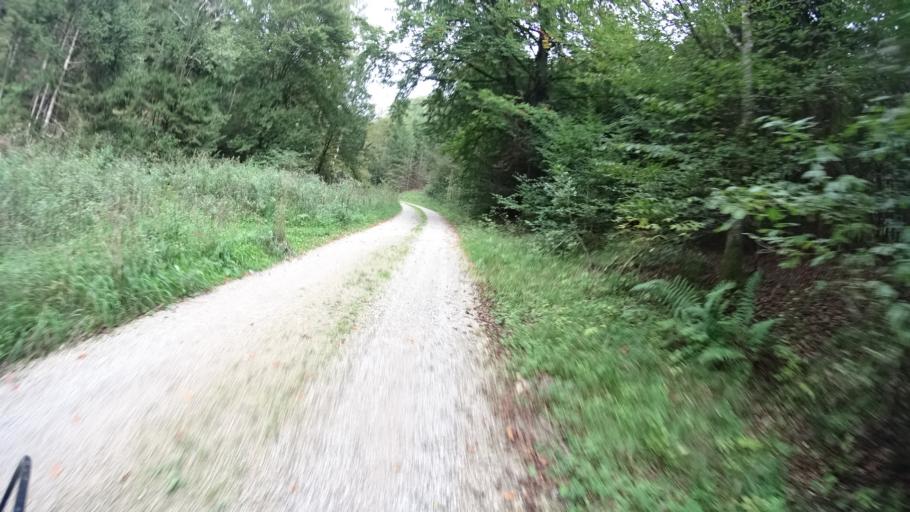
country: DE
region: Bavaria
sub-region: Upper Bavaria
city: Walting
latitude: 48.8987
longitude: 11.2983
